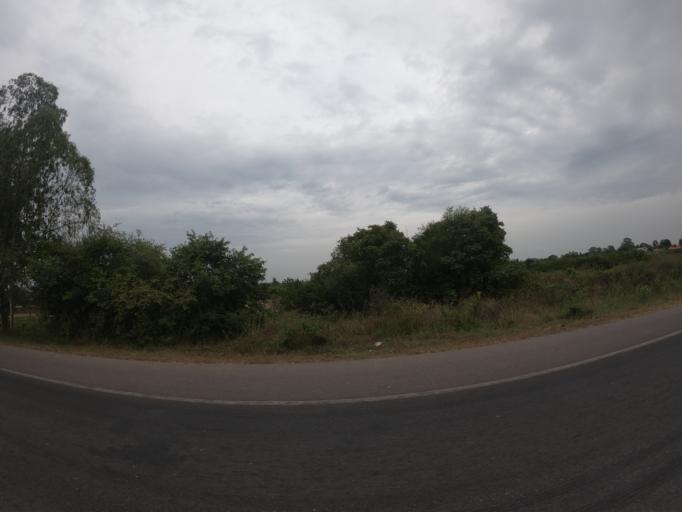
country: TH
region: Roi Et
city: Chiang Khwan
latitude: 16.1200
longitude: 103.8460
